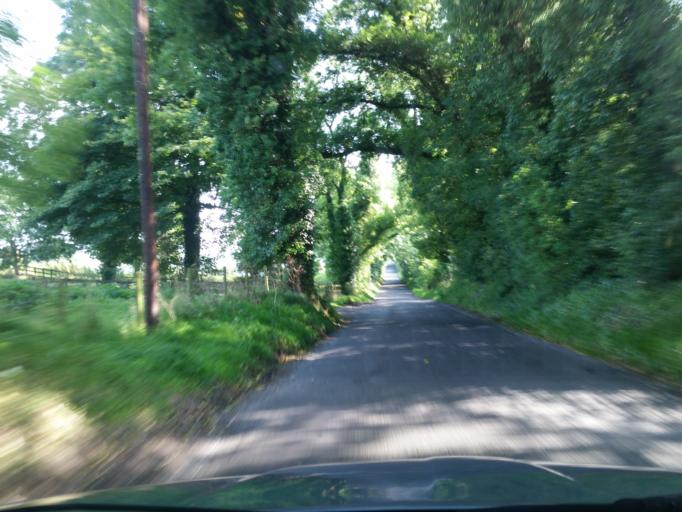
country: GB
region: Northern Ireland
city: Ballinamallard
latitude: 54.3849
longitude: -7.5696
